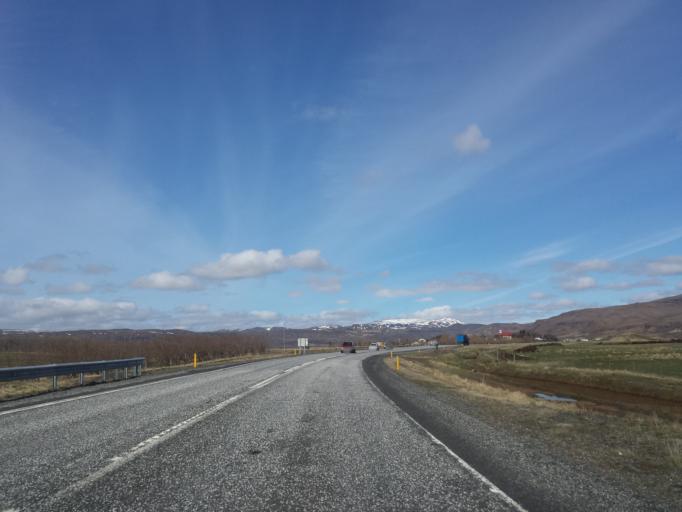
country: IS
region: South
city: Hveragerdi
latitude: 63.9655
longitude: -21.1335
